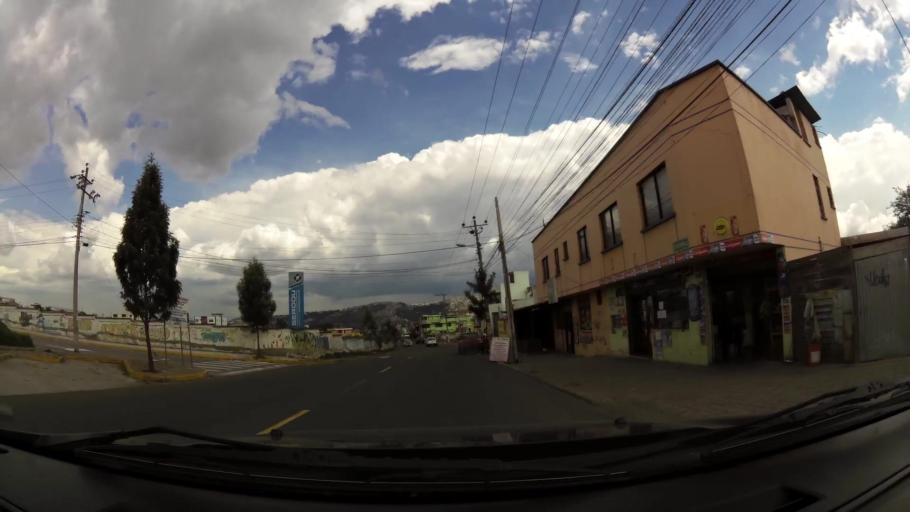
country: EC
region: Pichincha
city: Quito
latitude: -0.0928
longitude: -78.4426
